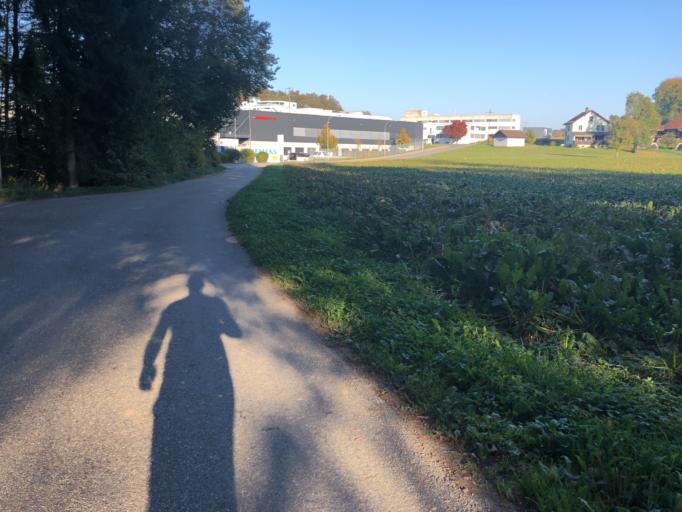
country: CH
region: Zurich
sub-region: Bezirk Uster
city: Kindhausen / Kindhausen (Dorf)
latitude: 47.4185
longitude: 8.6791
